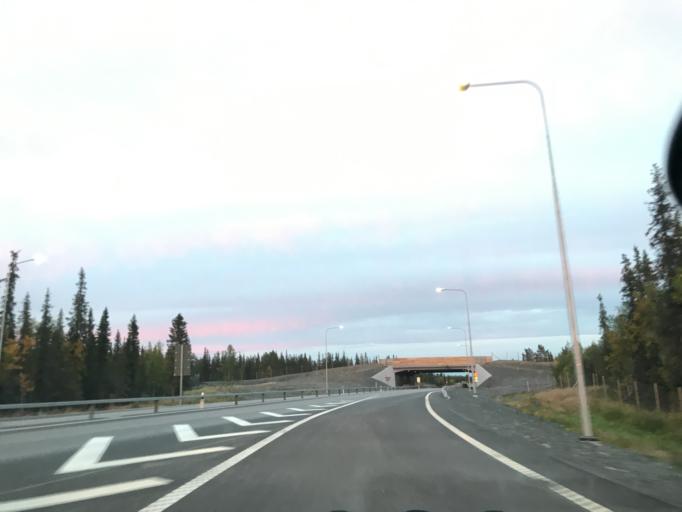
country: SE
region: Norrbotten
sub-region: Gallivare Kommun
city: Malmberget
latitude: 67.6943
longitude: 20.8094
